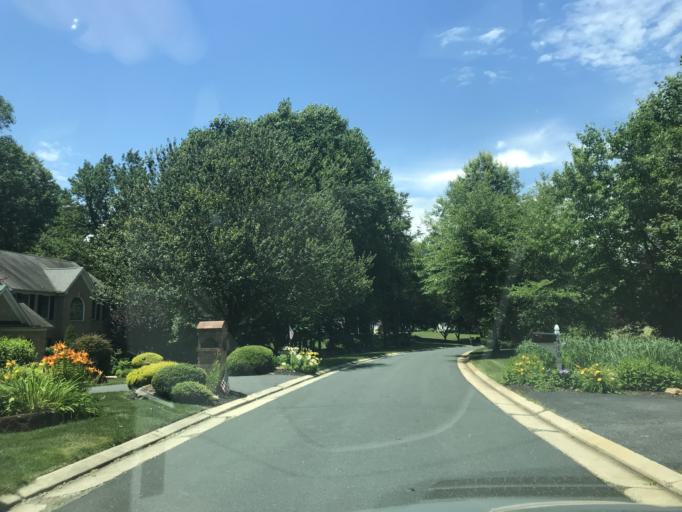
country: US
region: Maryland
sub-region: Baltimore County
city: Kingsville
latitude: 39.4704
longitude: -76.4578
